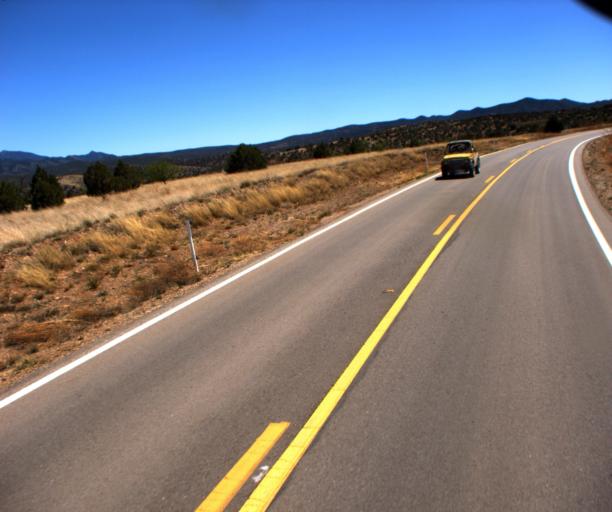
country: US
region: Arizona
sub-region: Cochise County
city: Huachuca City
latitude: 31.5313
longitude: -110.5019
